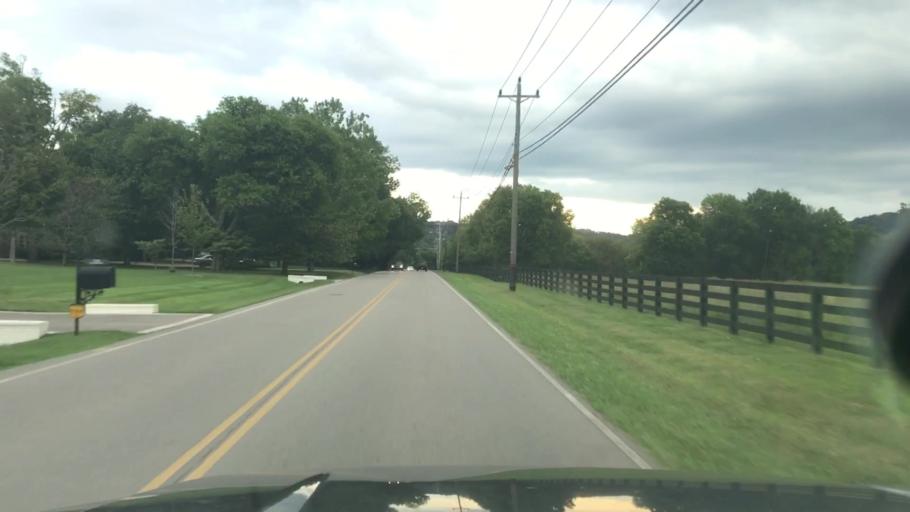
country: US
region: Tennessee
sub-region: Davidson County
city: Forest Hills
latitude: 36.0811
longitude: -86.8445
